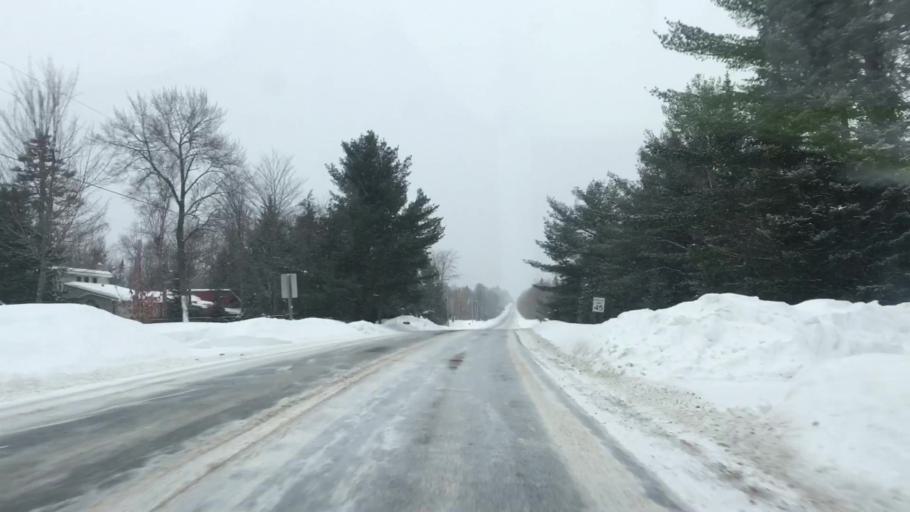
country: US
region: Maine
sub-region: Penobscot County
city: Medway
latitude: 45.5237
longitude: -68.3558
